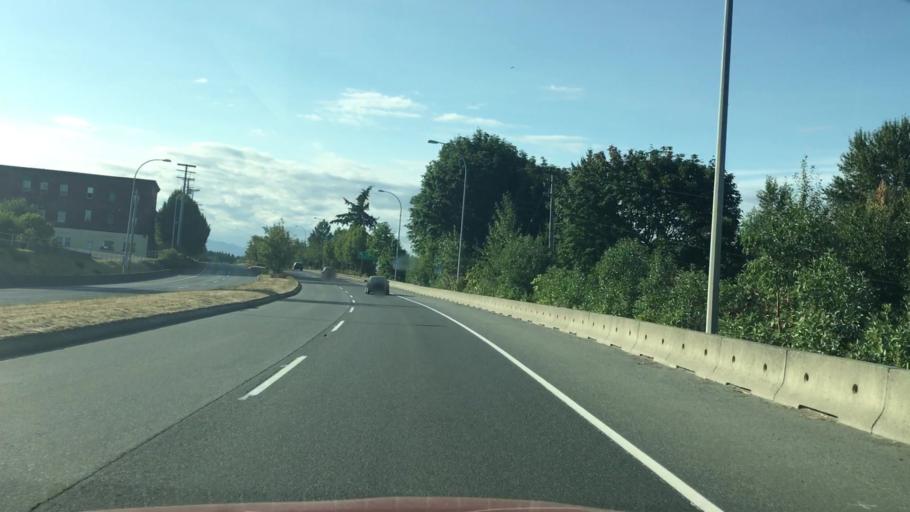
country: CA
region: British Columbia
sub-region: Cowichan Valley Regional District
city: Ladysmith
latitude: 48.9906
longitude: -123.8108
